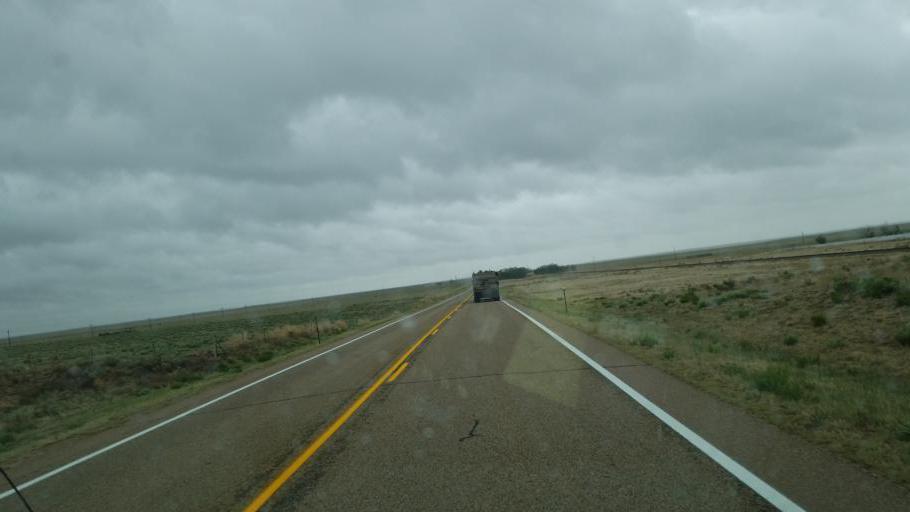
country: US
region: Colorado
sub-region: Kiowa County
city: Eads
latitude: 38.7855
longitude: -102.6962
